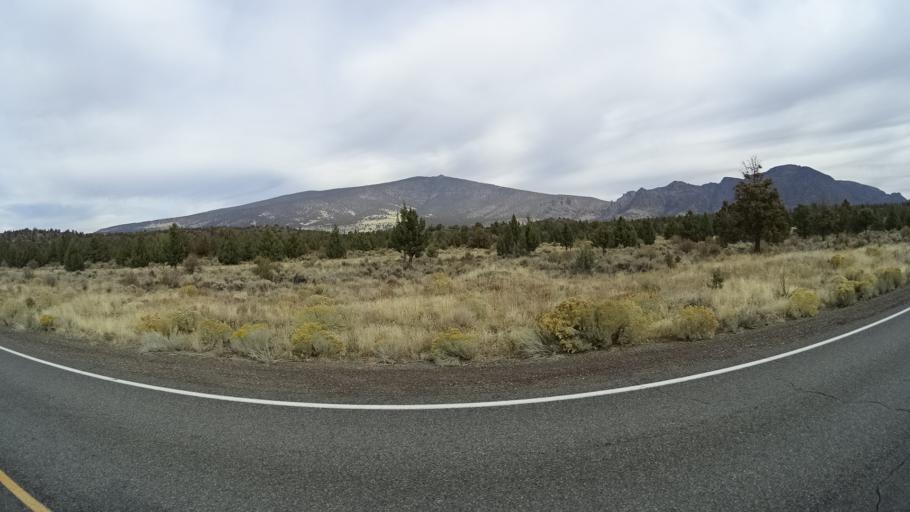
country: US
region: California
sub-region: Siskiyou County
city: Weed
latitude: 41.5728
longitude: -122.2762
